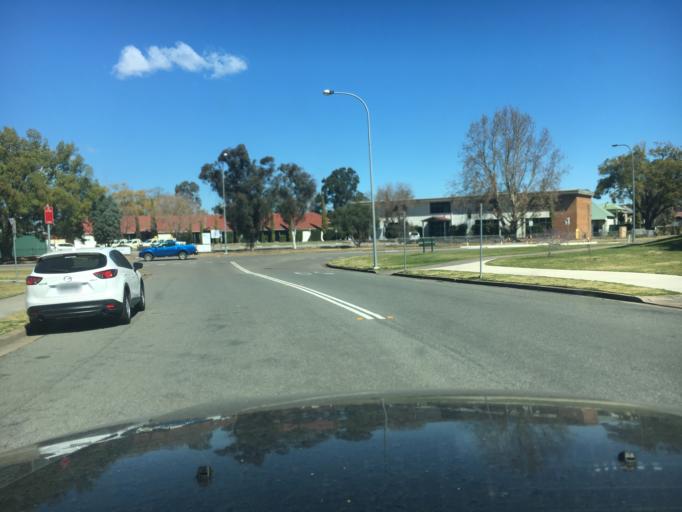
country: AU
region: New South Wales
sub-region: Singleton
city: Singleton
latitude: -32.5586
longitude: 151.1768
